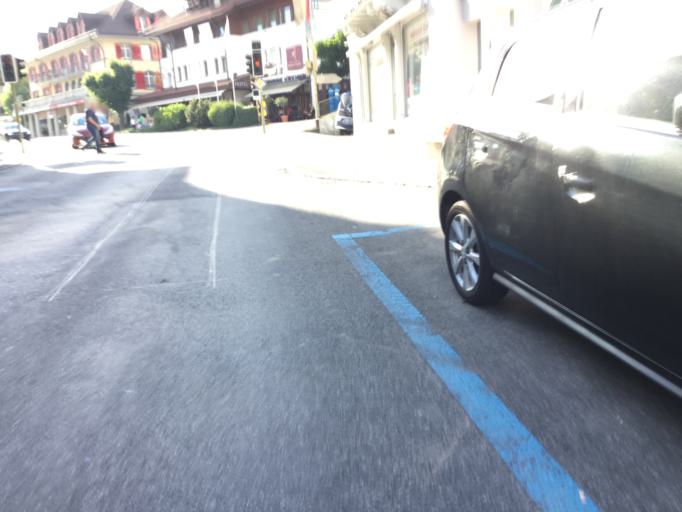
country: CH
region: Bern
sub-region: Frutigen-Niedersimmental District
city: Spiez
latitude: 46.6897
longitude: 7.6758
